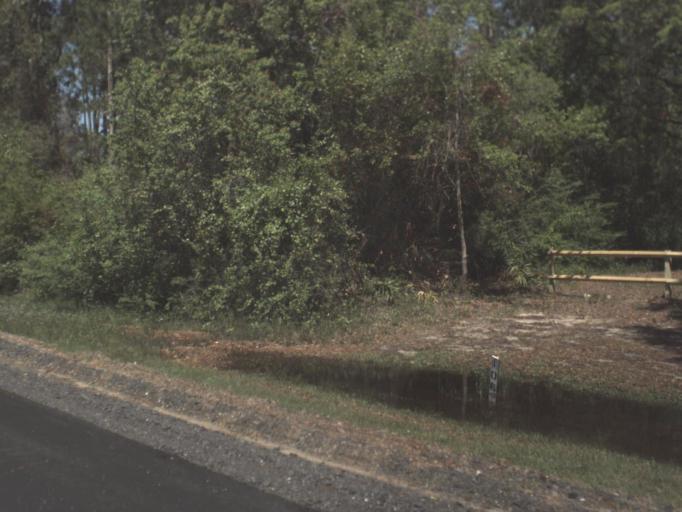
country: US
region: Florida
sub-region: Escambia County
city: Myrtle Grove
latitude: 30.4046
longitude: -87.3177
